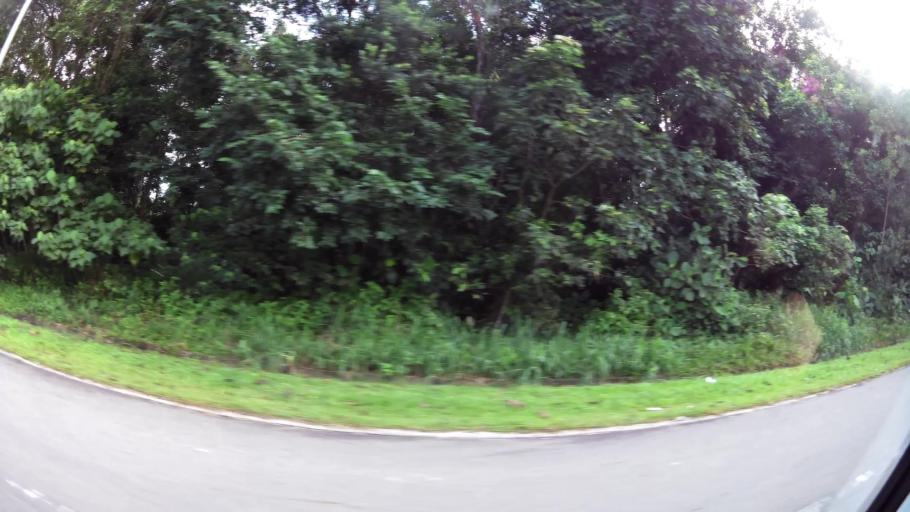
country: BN
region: Brunei and Muara
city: Bandar Seri Begawan
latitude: 4.8858
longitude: 114.9537
